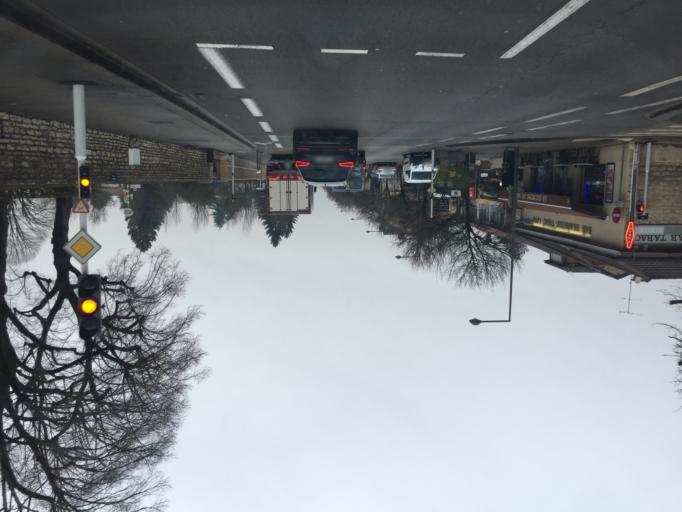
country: FR
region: Rhone-Alpes
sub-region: Departement de l'Ain
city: Bourg-en-Bresse
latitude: 46.1972
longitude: 5.2358
